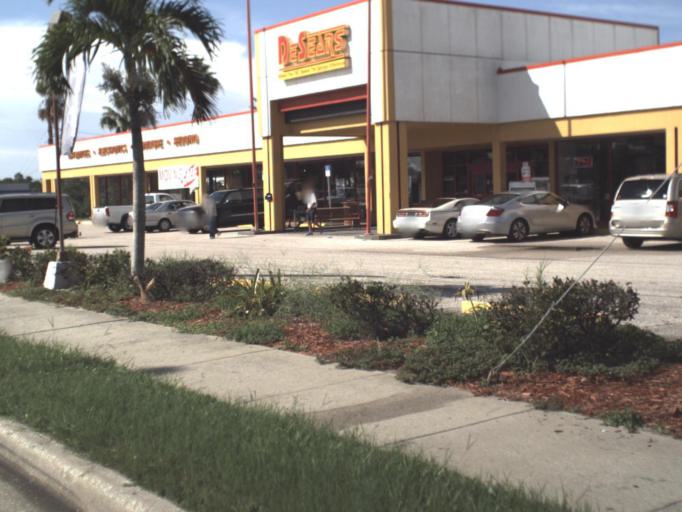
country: US
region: Florida
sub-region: Sarasota County
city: South Sarasota
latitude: 27.2868
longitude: -82.5308
